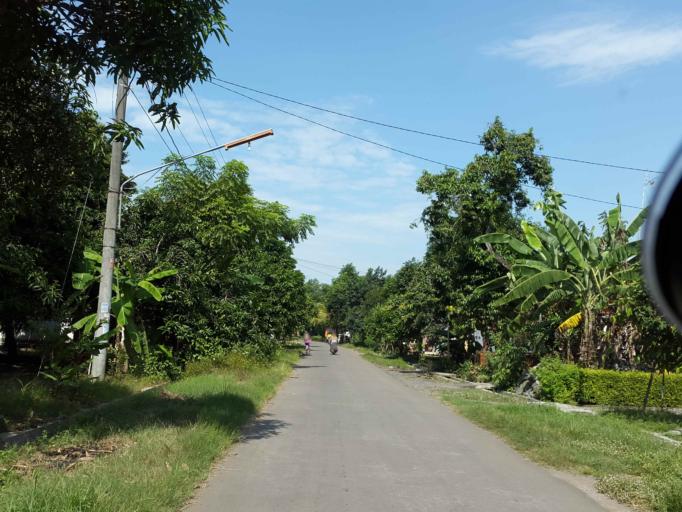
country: ID
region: Central Java
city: Petarukan
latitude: -6.8605
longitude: 109.4009
